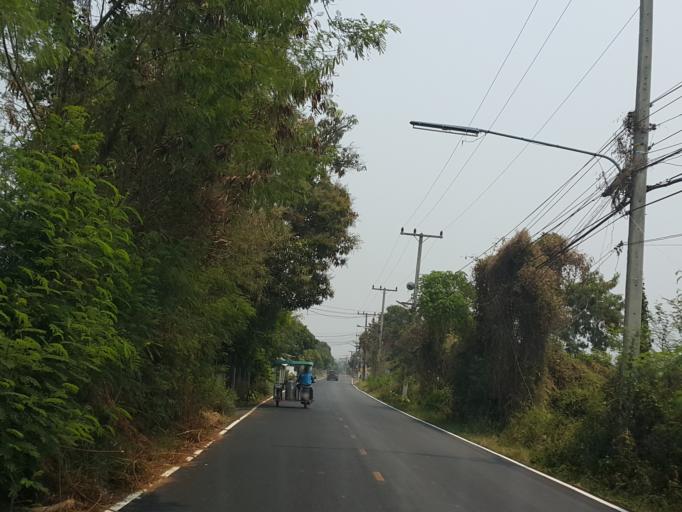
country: TH
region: Chiang Mai
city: San Kamphaeng
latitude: 18.7228
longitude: 99.1884
